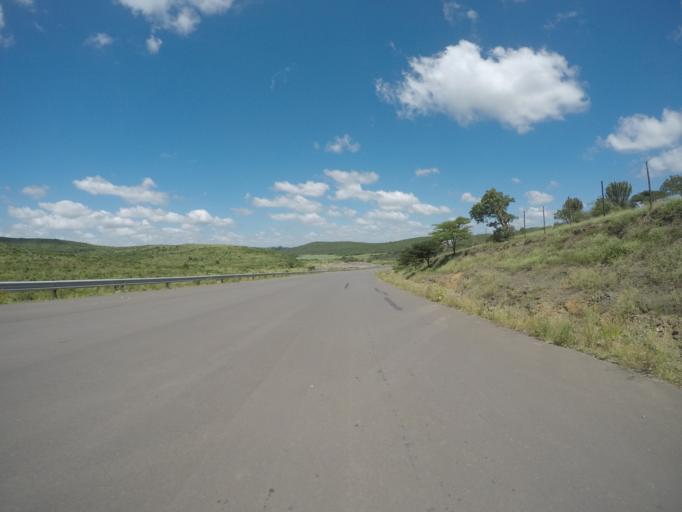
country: ZA
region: KwaZulu-Natal
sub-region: uThungulu District Municipality
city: Empangeni
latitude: -28.6150
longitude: 31.7540
